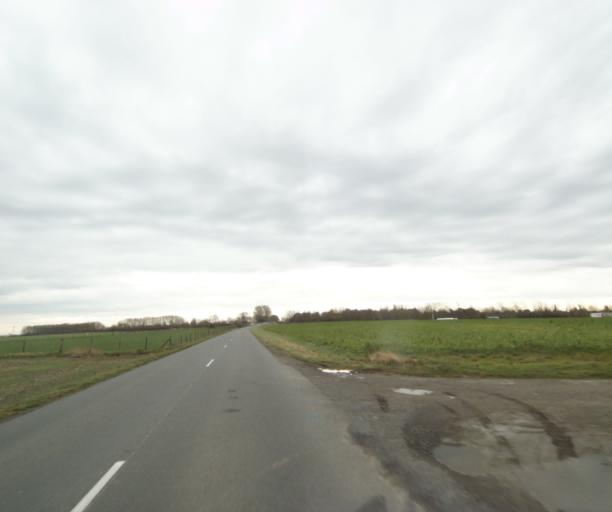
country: FR
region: Nord-Pas-de-Calais
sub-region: Departement du Nord
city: Saultain
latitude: 50.3594
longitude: 3.5812
